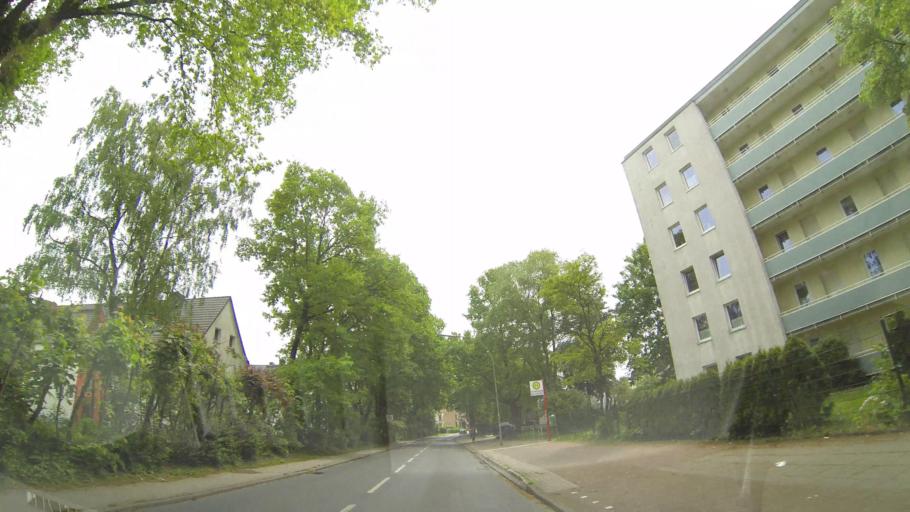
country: DE
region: Schleswig-Holstein
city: Halstenbek
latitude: 53.6025
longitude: 9.8459
